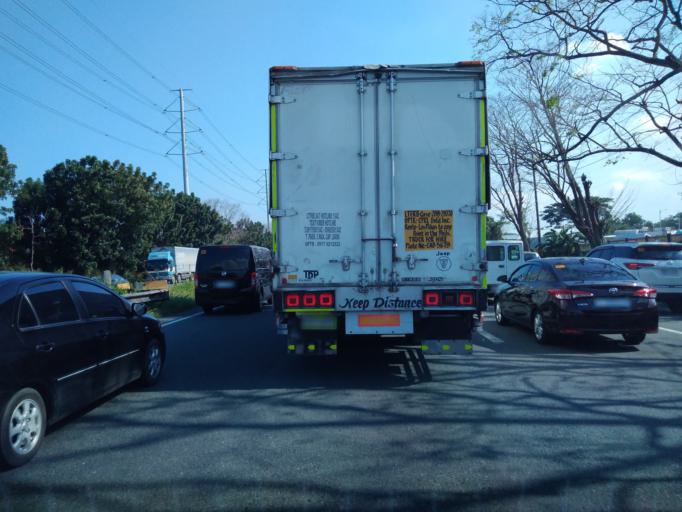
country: PH
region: Calabarzon
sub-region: Province of Laguna
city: Prinza
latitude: 14.2244
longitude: 121.1219
